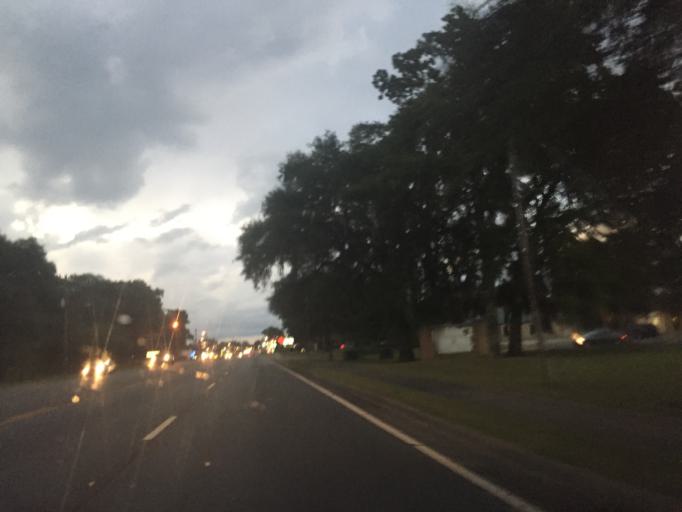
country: US
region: Georgia
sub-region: Liberty County
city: Hinesville
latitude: 31.8498
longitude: -81.5867
